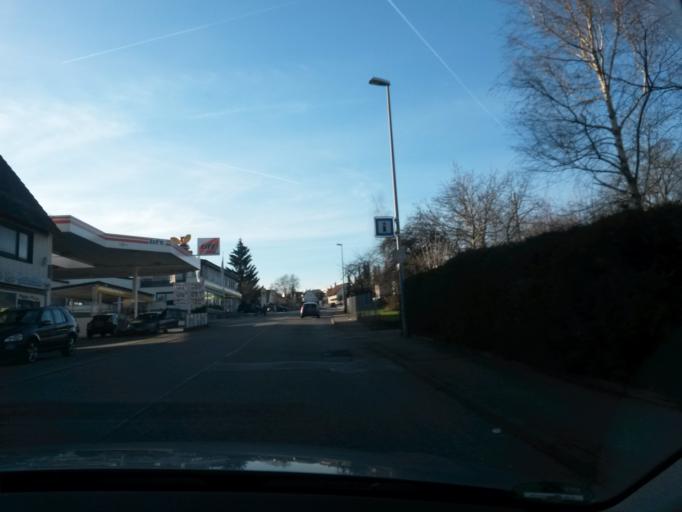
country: DE
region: Baden-Wuerttemberg
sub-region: Karlsruhe Region
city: Birkenfeld
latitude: 48.8708
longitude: 8.6323
